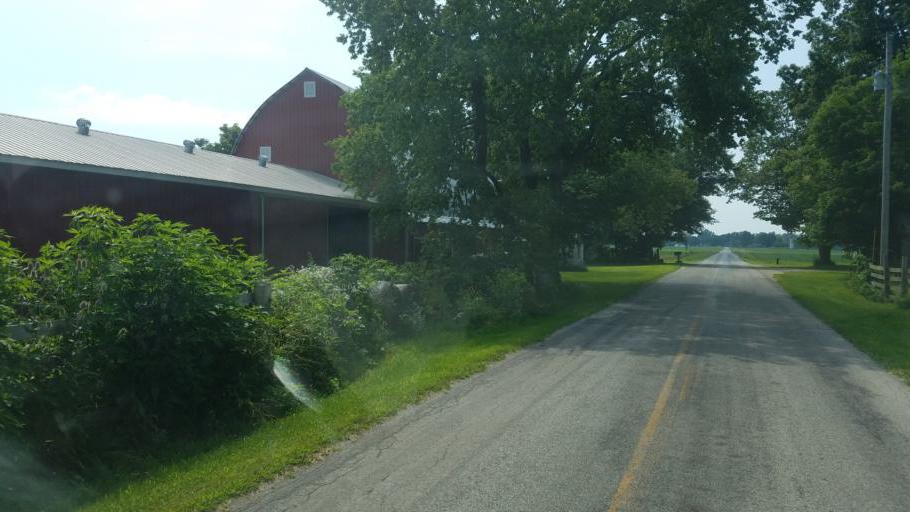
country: US
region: Ohio
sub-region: Union County
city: Richwood
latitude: 40.5924
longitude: -83.3962
